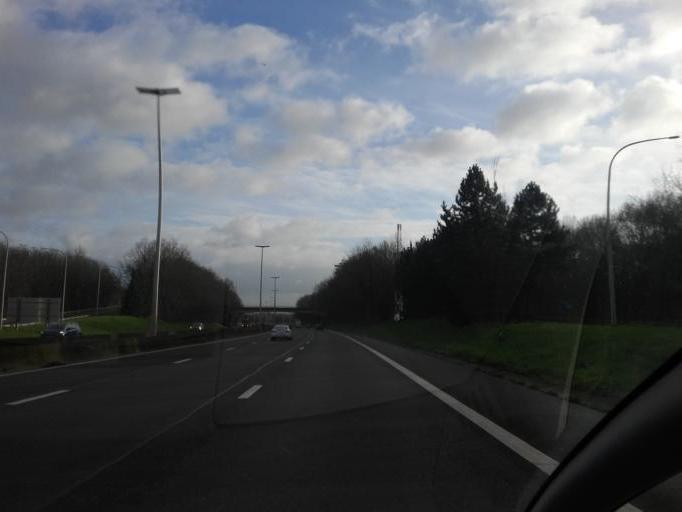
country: BE
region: Wallonia
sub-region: Province du Brabant Wallon
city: Louvain-la-Neuve
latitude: 50.6637
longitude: 4.6438
